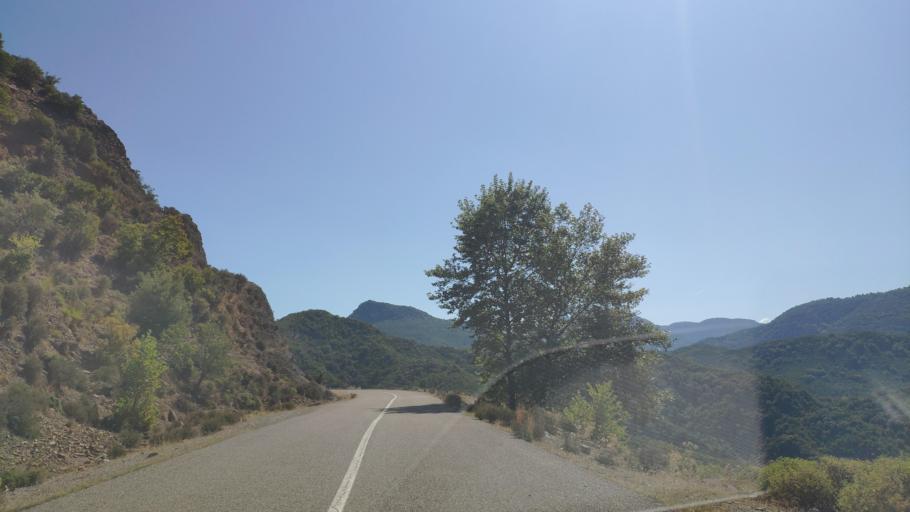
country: GR
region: Central Greece
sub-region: Nomos Evrytanias
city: Kerasochori
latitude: 38.9916
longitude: 21.5096
